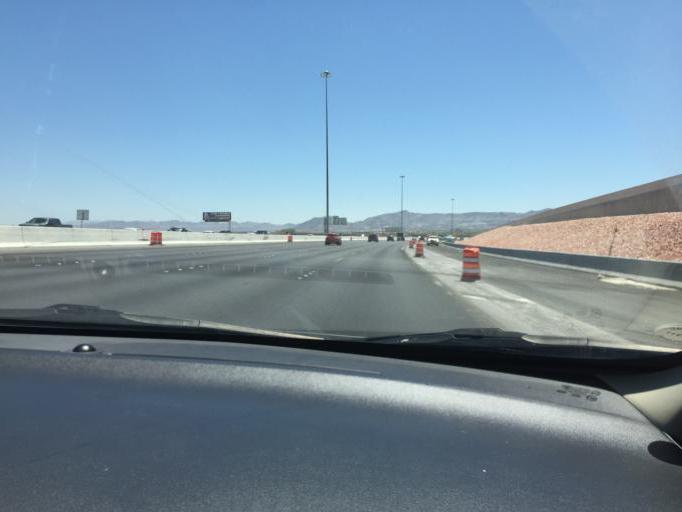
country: US
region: Nevada
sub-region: Clark County
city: Paradise
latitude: 36.0615
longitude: -115.1462
